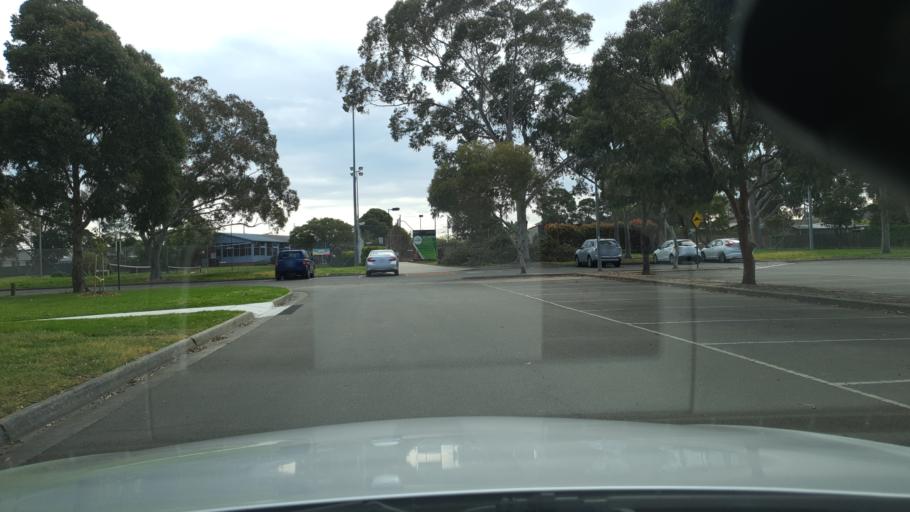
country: AU
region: Victoria
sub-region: Greater Dandenong
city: Noble Park North
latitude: -37.9332
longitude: 145.1779
